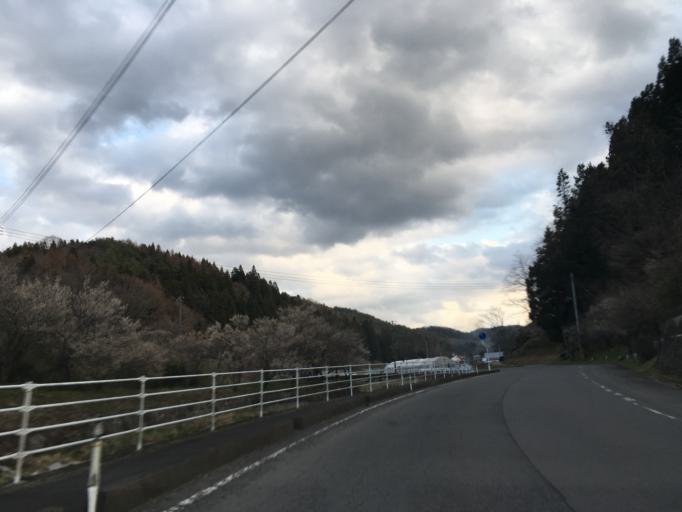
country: JP
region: Fukushima
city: Ishikawa
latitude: 37.0580
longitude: 140.5099
